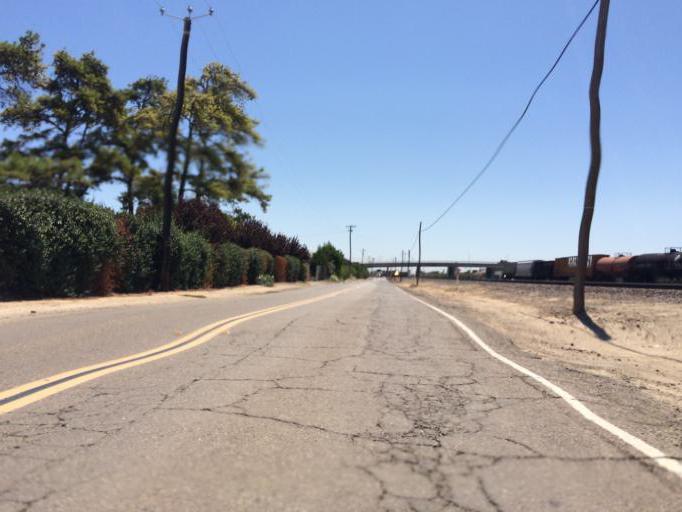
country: US
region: California
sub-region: Fresno County
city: Fresno
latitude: 36.7103
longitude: -119.7685
